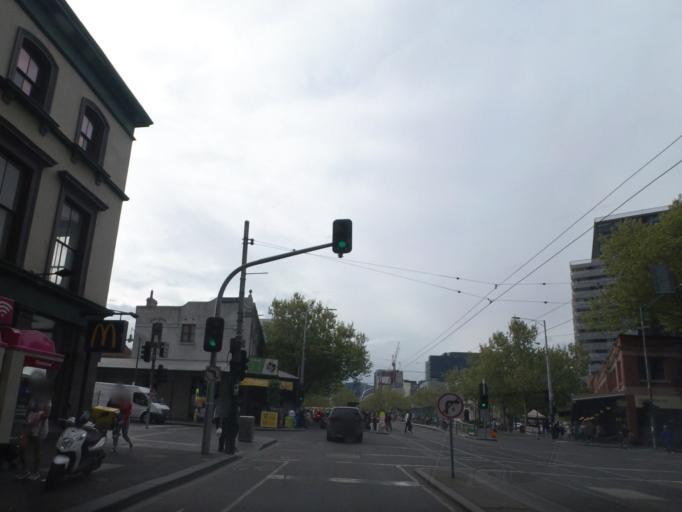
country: AU
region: Victoria
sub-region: Melbourne
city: Melbourne
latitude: -37.8075
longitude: 144.9600
